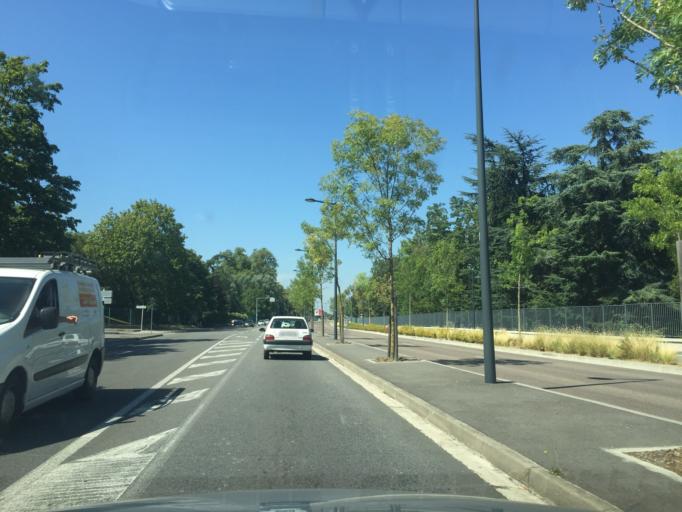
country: FR
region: Midi-Pyrenees
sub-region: Departement de la Haute-Garonne
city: Ramonville-Saint-Agne
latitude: 43.5576
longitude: 1.4648
